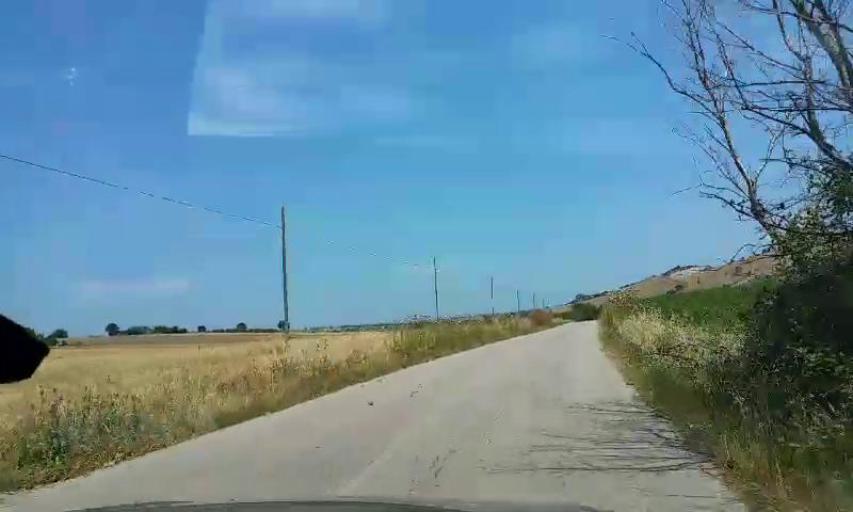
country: IT
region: Molise
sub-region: Provincia di Campobasso
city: Guglionesi
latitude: 41.9487
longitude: 14.9011
